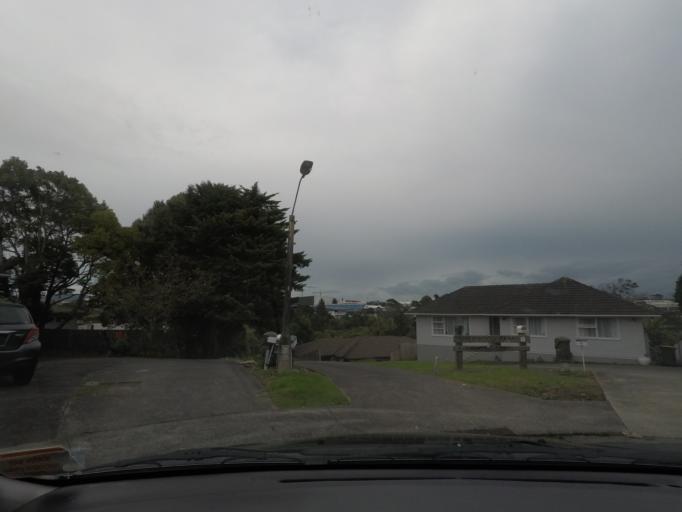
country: NZ
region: Auckland
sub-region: Auckland
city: Rosebank
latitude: -36.8567
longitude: 174.6414
